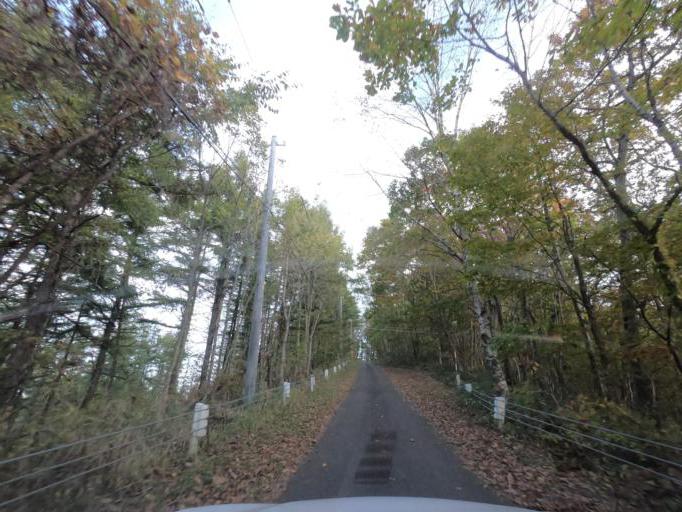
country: JP
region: Hokkaido
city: Obihiro
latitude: 42.5846
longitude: 143.3134
